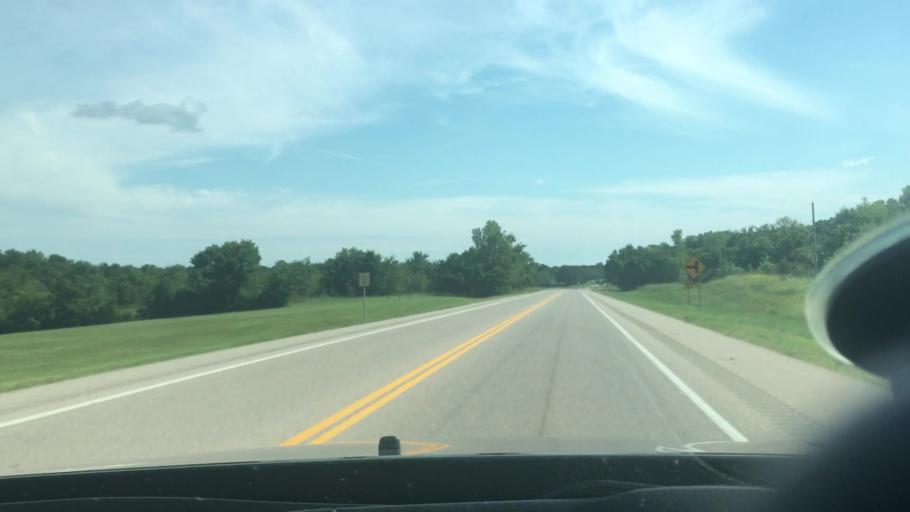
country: US
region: Oklahoma
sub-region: Seminole County
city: Seminole
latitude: 35.1534
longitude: -96.6748
